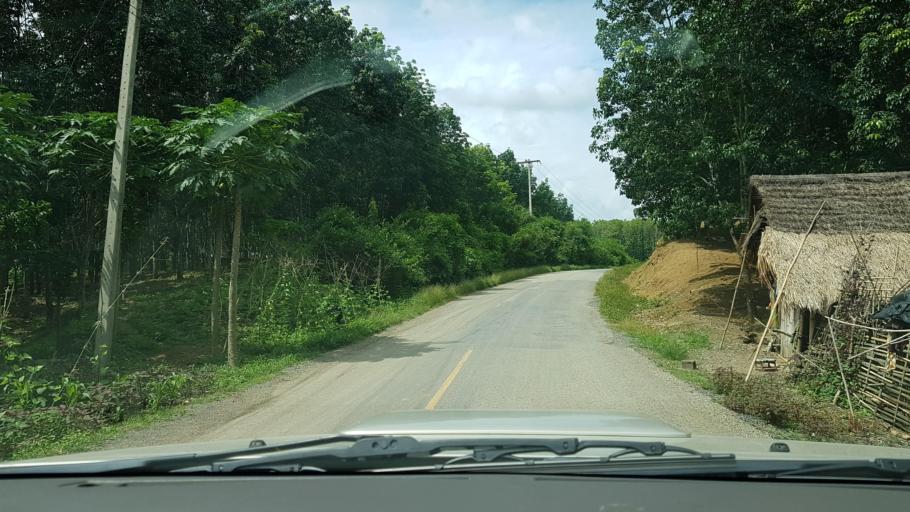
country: LA
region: Loungnamtha
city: Muang Nale
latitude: 20.2323
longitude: 101.5641
